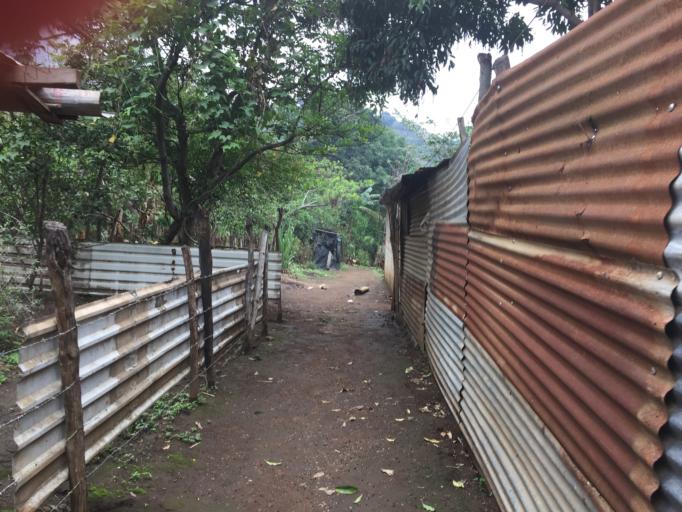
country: GT
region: Sacatepequez
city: Magdalena Milpas Altas
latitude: 14.5107
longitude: -90.6515
